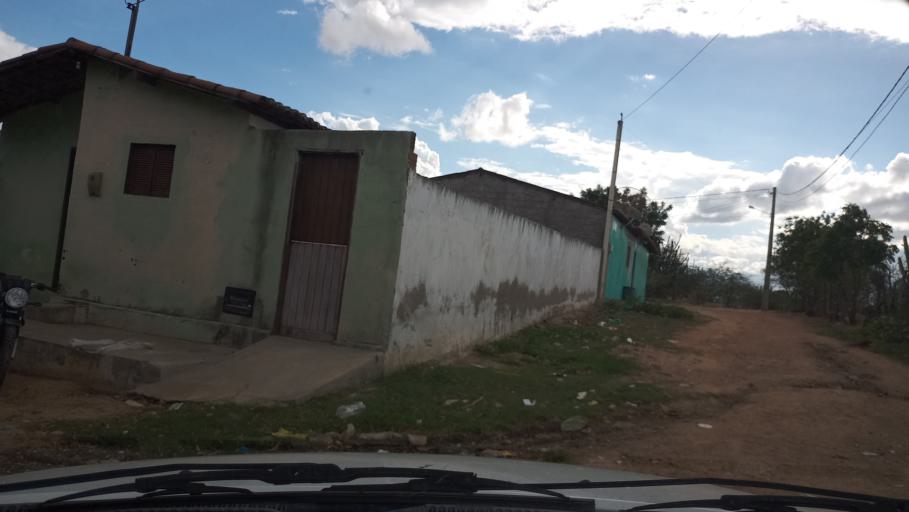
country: BR
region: Rio Grande do Norte
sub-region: Sao Tome
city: Sao Tome
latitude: -5.9414
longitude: -35.9270
